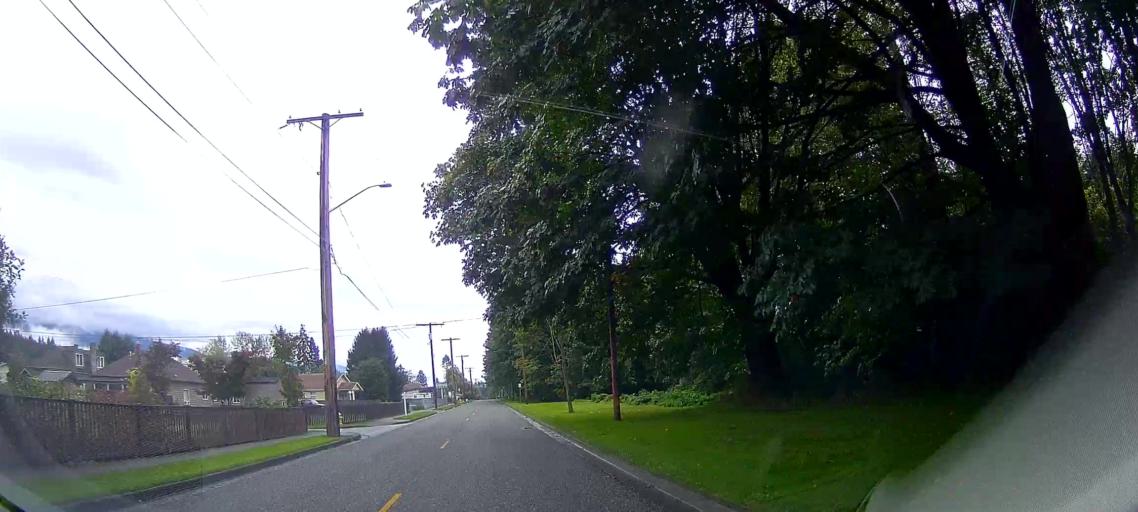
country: US
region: Washington
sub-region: Skagit County
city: Sedro-Woolley
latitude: 48.5262
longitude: -122.0647
